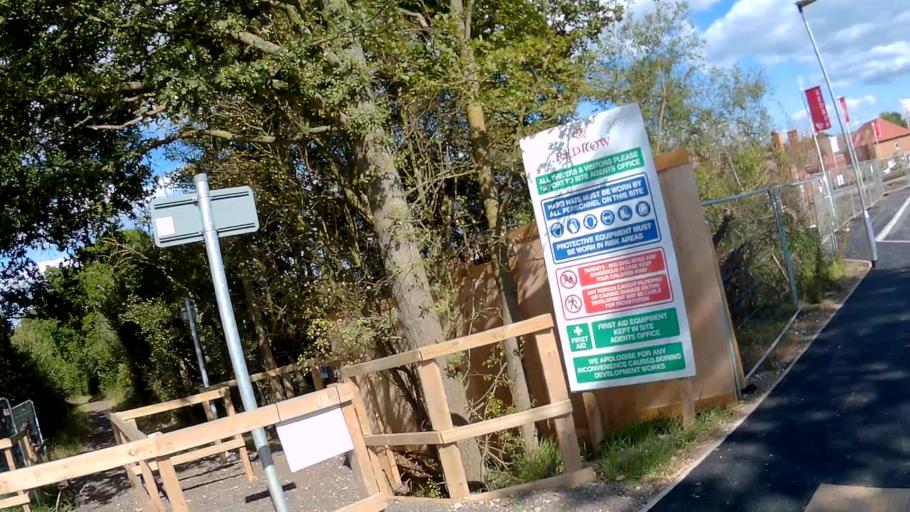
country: GB
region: England
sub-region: Bracknell Forest
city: Bracknell
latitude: 51.4335
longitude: -0.7500
